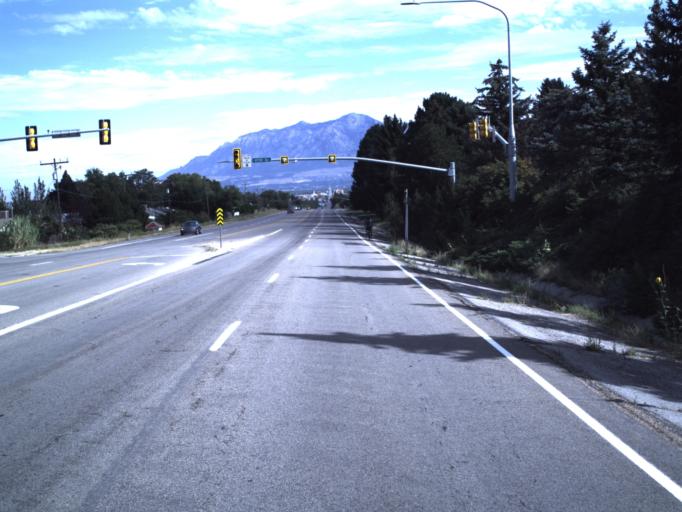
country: US
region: Utah
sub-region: Weber County
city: Washington Terrace
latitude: 41.1769
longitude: -111.9714
